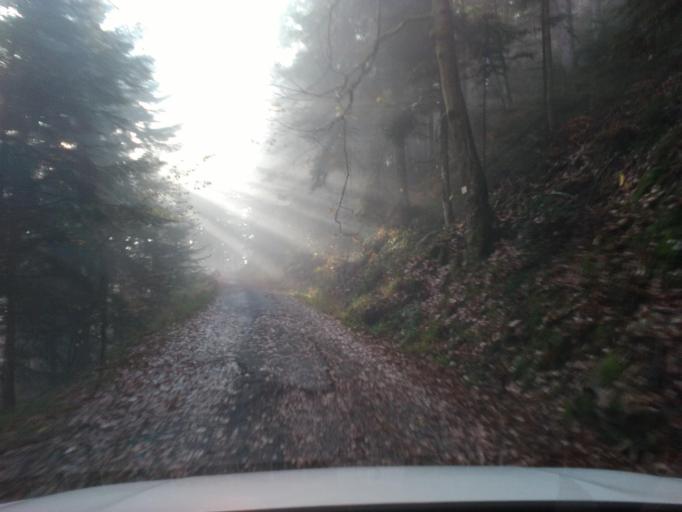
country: FR
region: Lorraine
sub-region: Departement des Vosges
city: Senones
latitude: 48.4124
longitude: 6.9739
